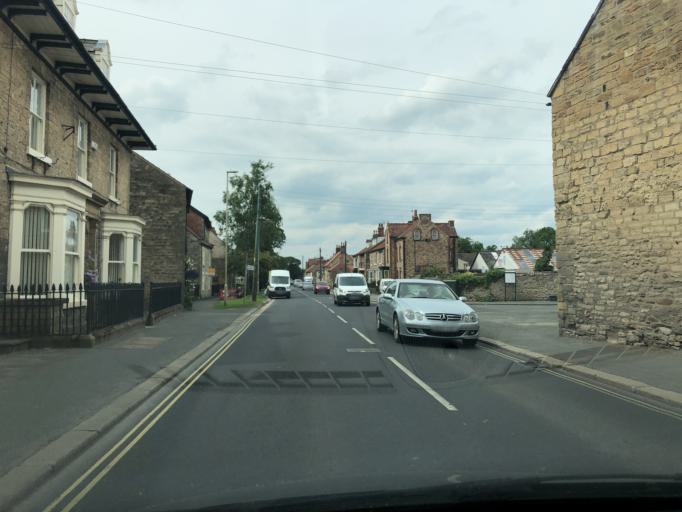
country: GB
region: England
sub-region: North Yorkshire
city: Pickering
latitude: 54.2454
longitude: -0.7827
